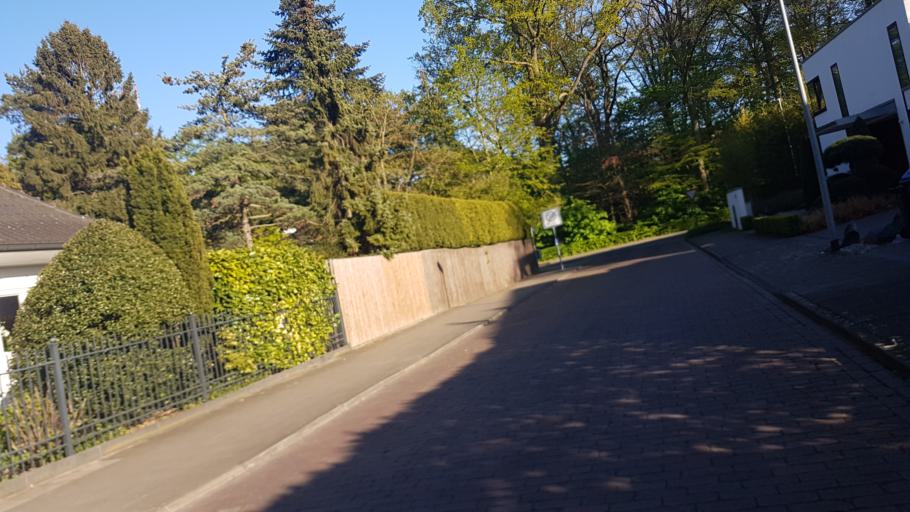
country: DE
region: Lower Saxony
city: Hannover
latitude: 52.3951
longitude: 9.7876
